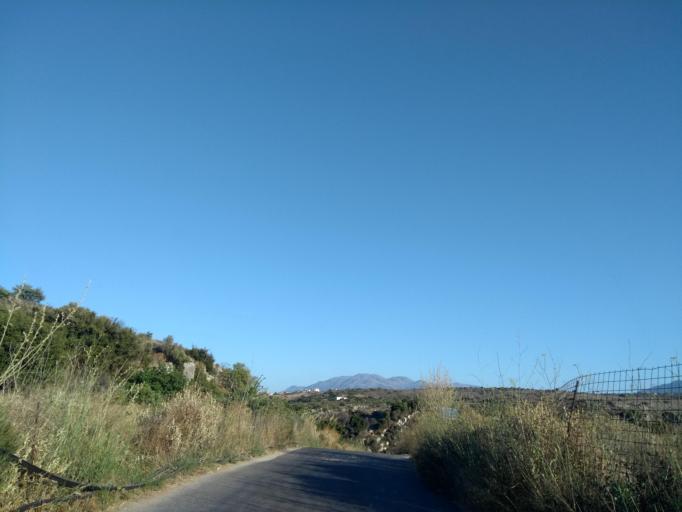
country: GR
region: Crete
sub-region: Nomos Chanias
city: Kalivai
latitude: 35.4308
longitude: 24.1768
